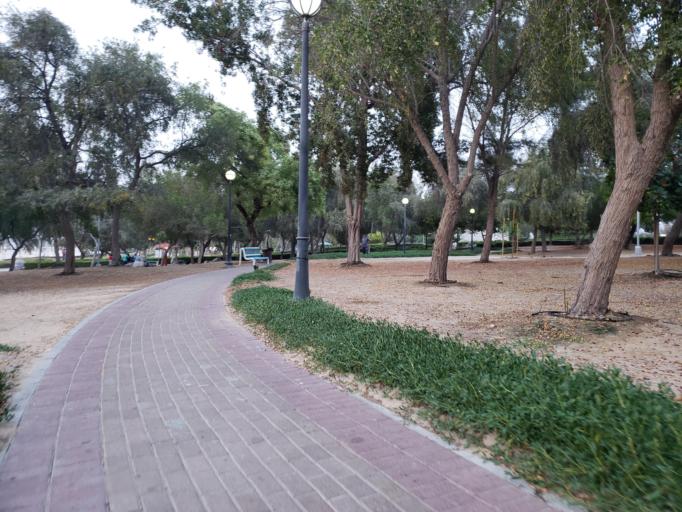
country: AE
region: Ash Shariqah
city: Sharjah
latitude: 25.3197
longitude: 55.3472
